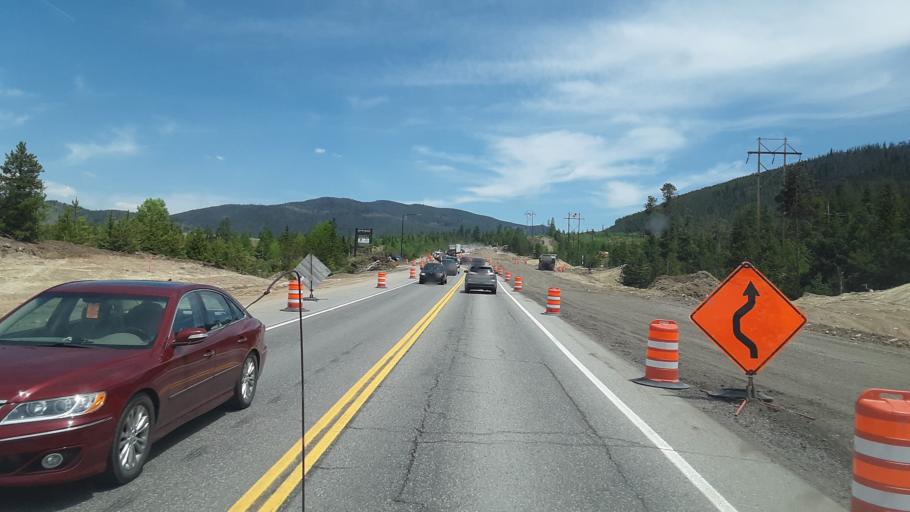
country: US
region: Colorado
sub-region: Summit County
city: Frisco
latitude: 39.5730
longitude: -106.0795
